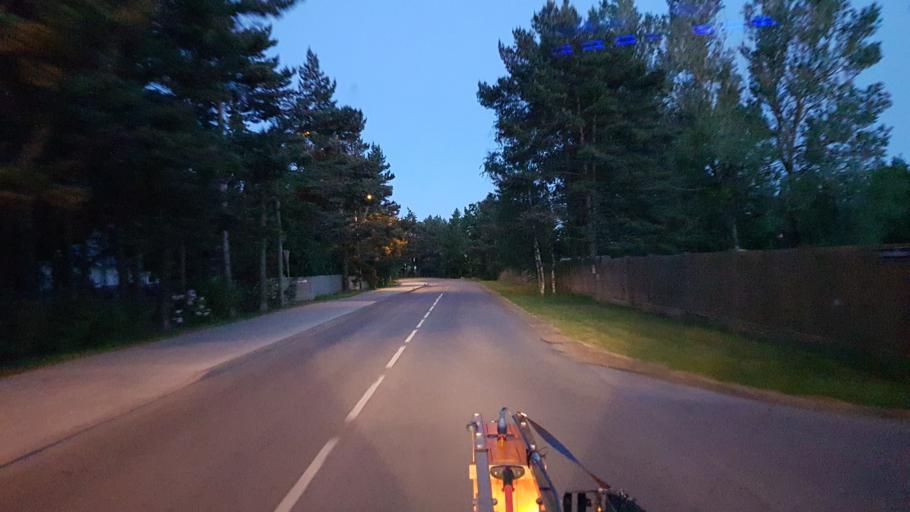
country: EE
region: Harju
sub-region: Harku vald
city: Tabasalu
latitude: 59.4468
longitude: 24.5911
